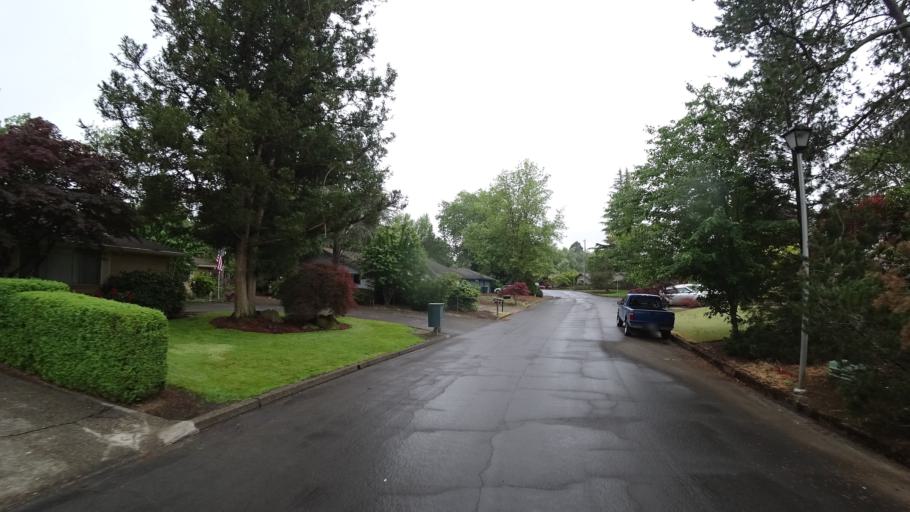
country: US
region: Oregon
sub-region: Washington County
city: Garden Home-Whitford
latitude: 45.4690
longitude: -122.7669
